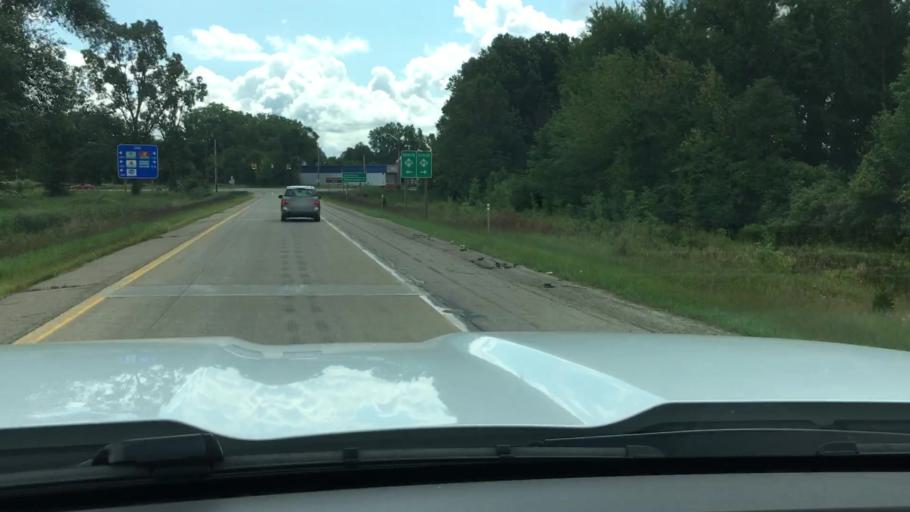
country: US
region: Michigan
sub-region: Eaton County
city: Dimondale
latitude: 42.6644
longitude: -84.5926
